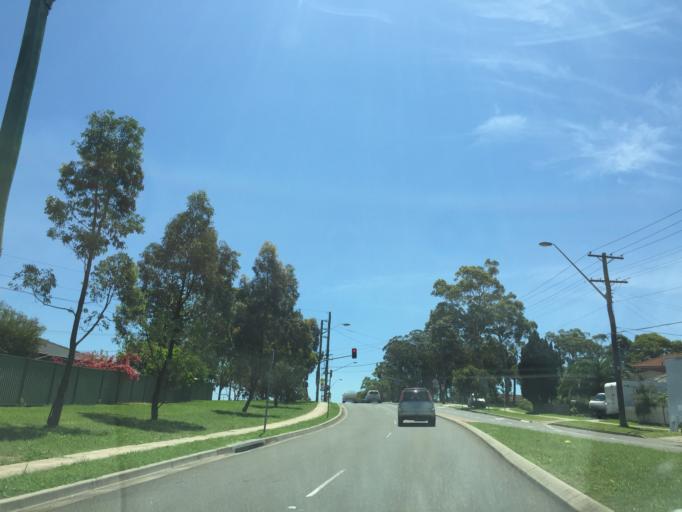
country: AU
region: New South Wales
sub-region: Blacktown
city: Blacktown
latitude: -33.7850
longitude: 150.9265
